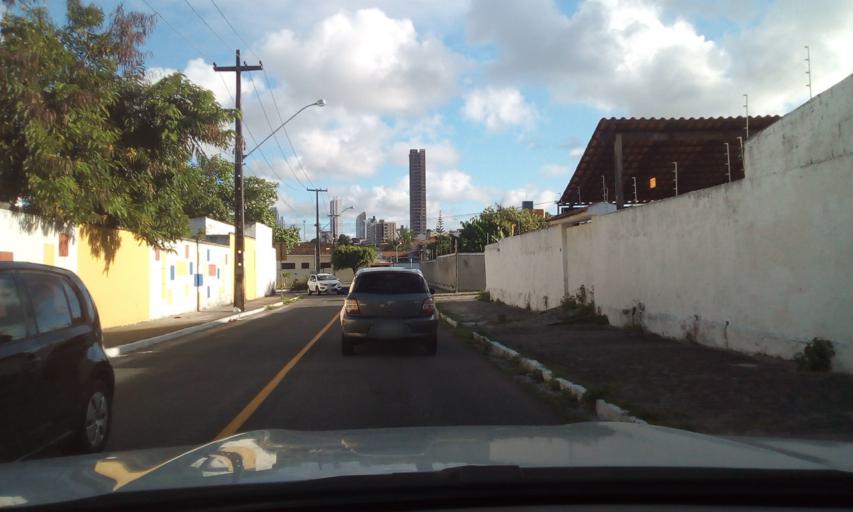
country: BR
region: Paraiba
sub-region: Joao Pessoa
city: Joao Pessoa
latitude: -7.0994
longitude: -34.8545
